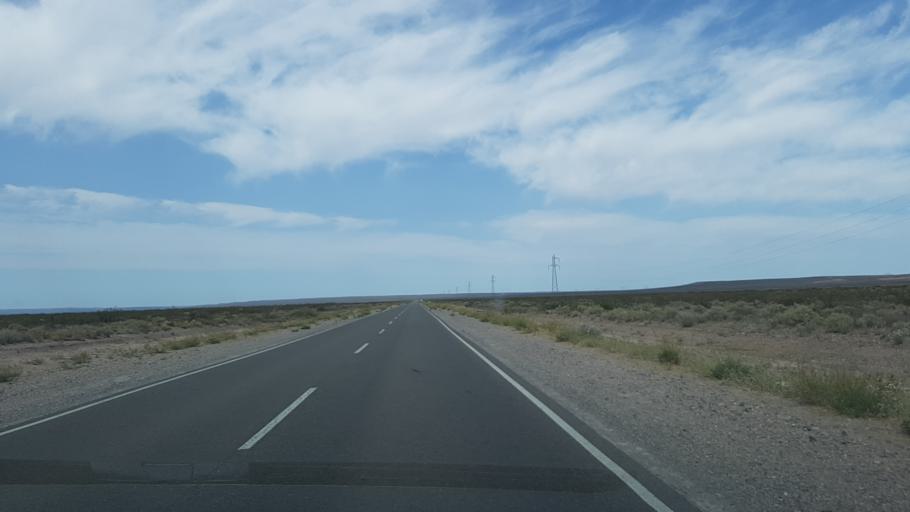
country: AR
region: Neuquen
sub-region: Departamento de Picun Leufu
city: Picun Leufu
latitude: -39.6681
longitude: -69.4389
